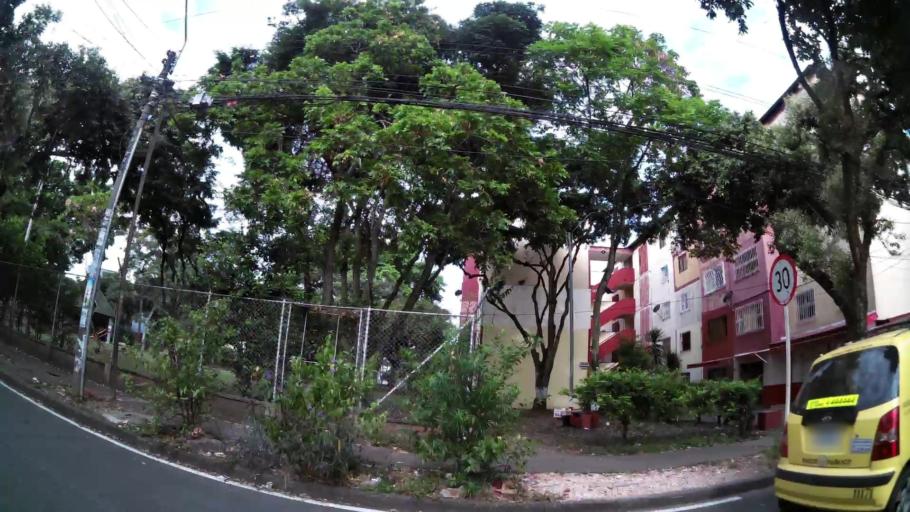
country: CO
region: Valle del Cauca
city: Cali
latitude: 3.4768
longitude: -76.4934
